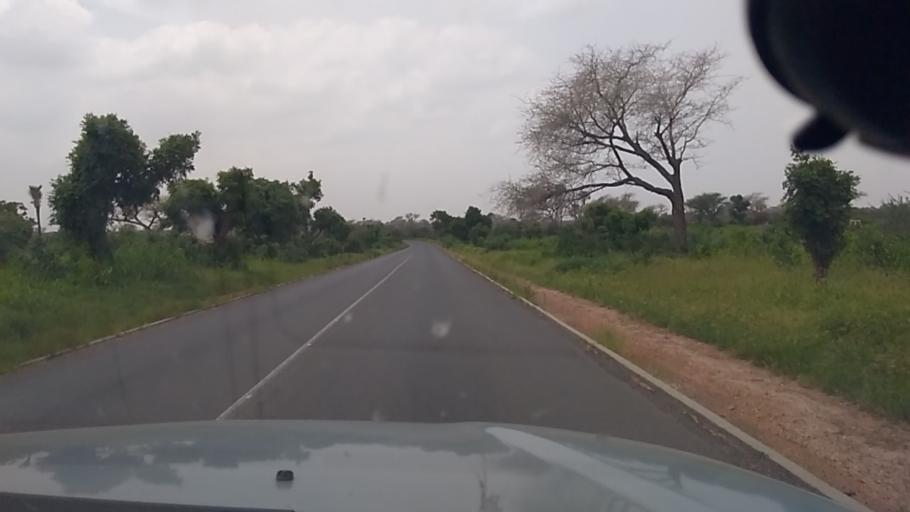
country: SN
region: Thies
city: Mekhe
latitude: 14.9844
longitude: -16.7632
